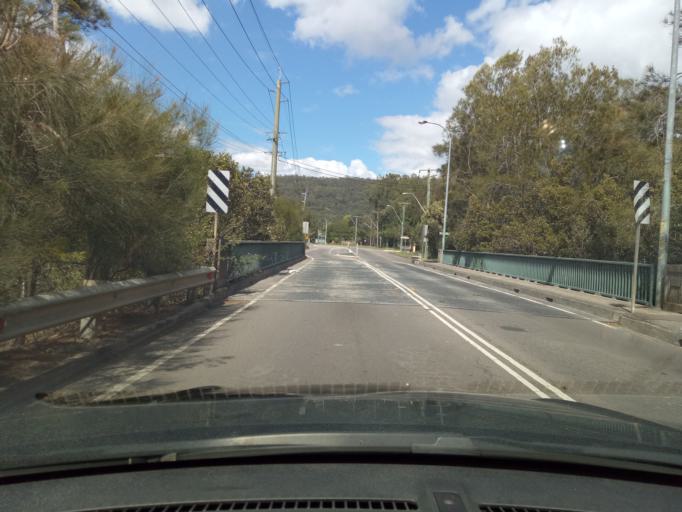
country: AU
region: New South Wales
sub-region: Gosford Shire
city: Point Clare
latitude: -33.4316
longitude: 151.3162
